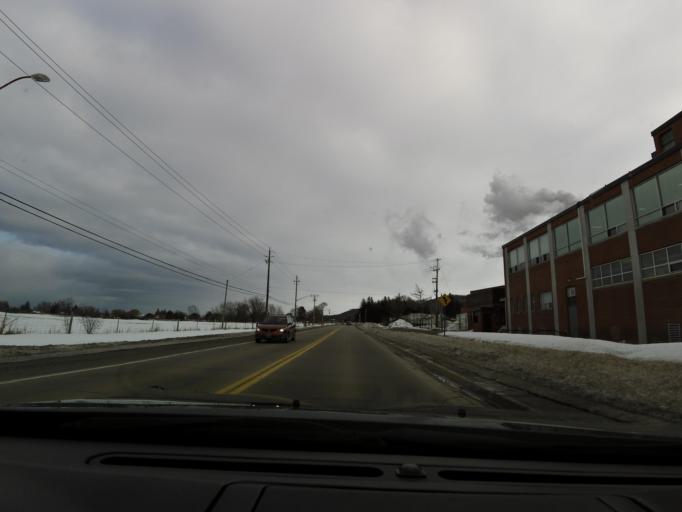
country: CA
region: Ontario
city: Hamilton
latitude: 43.2087
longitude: -79.6784
